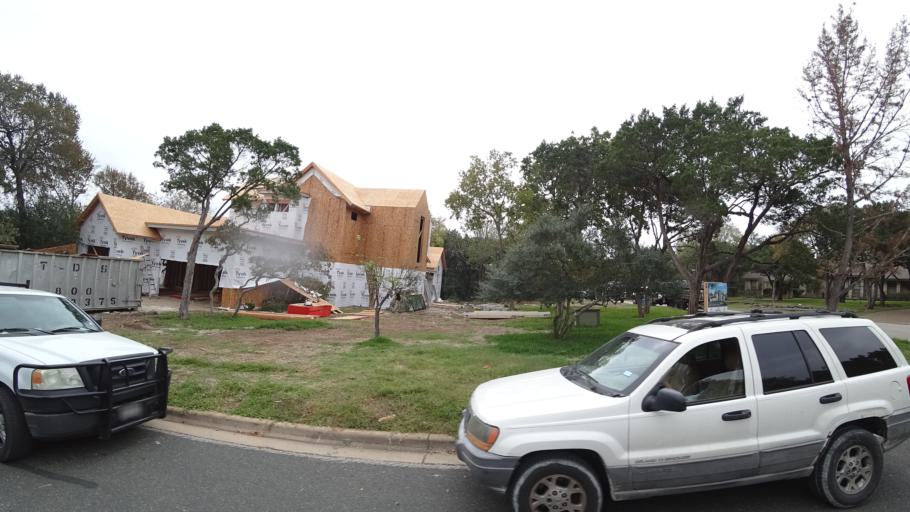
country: US
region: Texas
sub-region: Williamson County
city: Anderson Mill
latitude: 30.4418
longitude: -97.8193
